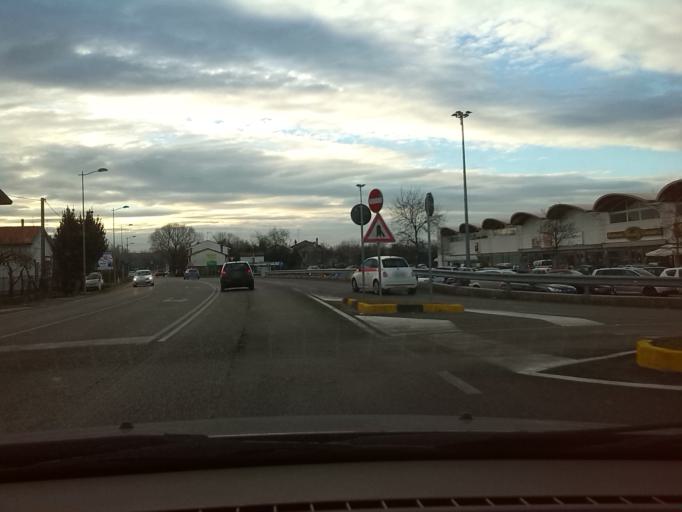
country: IT
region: Friuli Venezia Giulia
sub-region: Provincia di Gorizia
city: Sagrado
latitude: 45.8844
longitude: 13.4806
